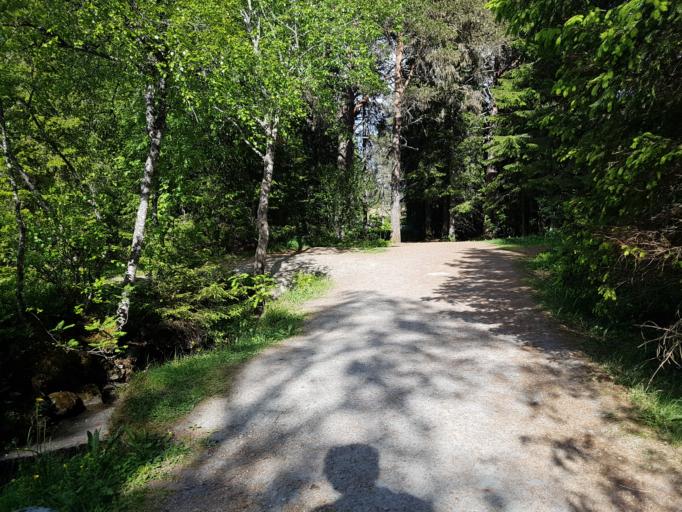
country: NO
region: Sor-Trondelag
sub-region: Trondheim
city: Trondheim
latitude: 63.3980
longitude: 10.3186
